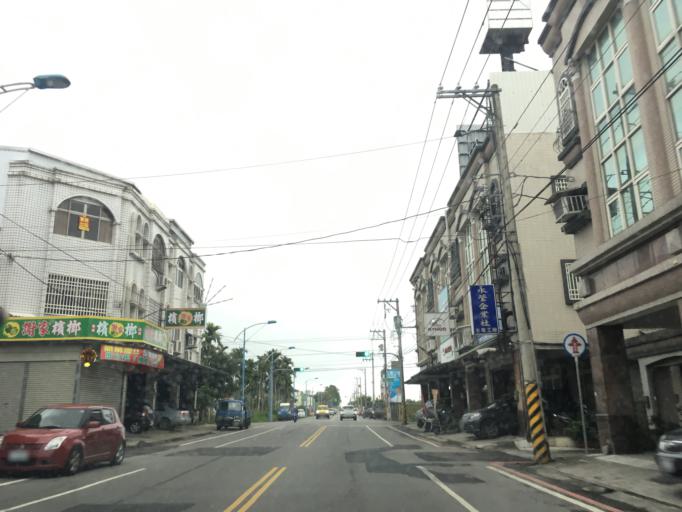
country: TW
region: Taiwan
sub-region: Hualien
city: Hualian
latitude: 23.9810
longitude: 121.5681
